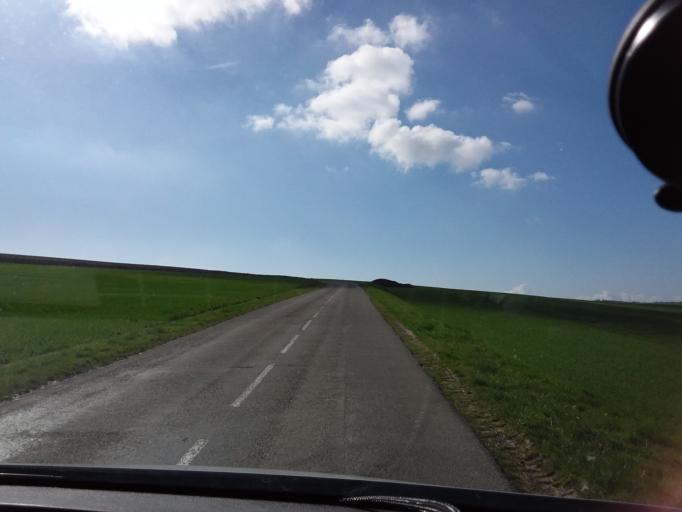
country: FR
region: Picardie
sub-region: Departement de l'Aisne
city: Origny-en-Thierache
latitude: 49.7947
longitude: 4.0092
